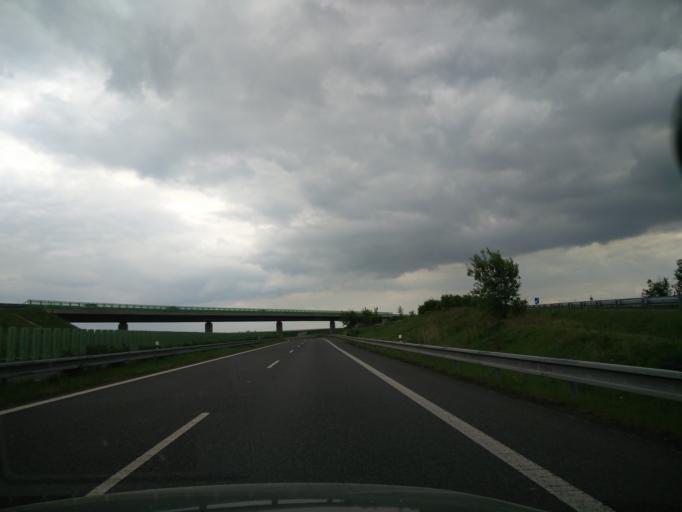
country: CZ
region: Jihocesky
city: Mirotice
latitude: 49.3530
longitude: 14.0544
